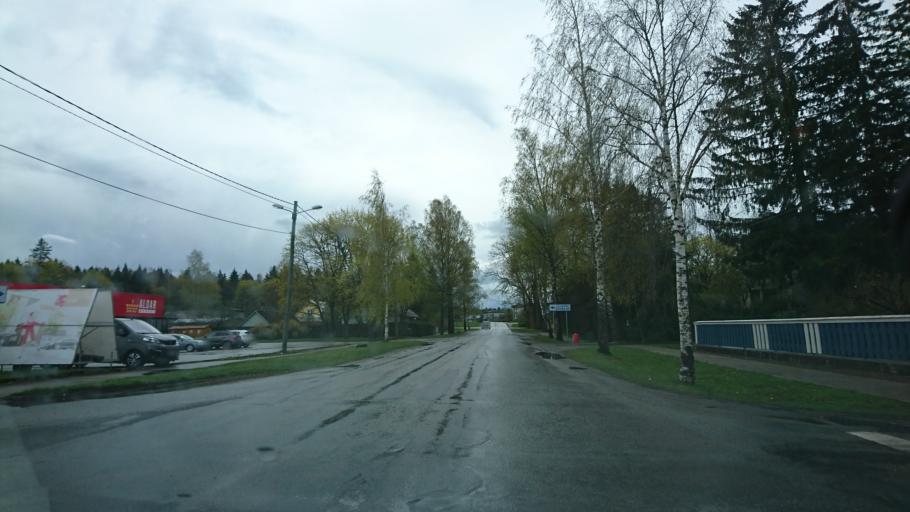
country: EE
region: Laeaene-Virumaa
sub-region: Rakvere linn
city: Rakvere
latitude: 59.3282
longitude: 26.3638
